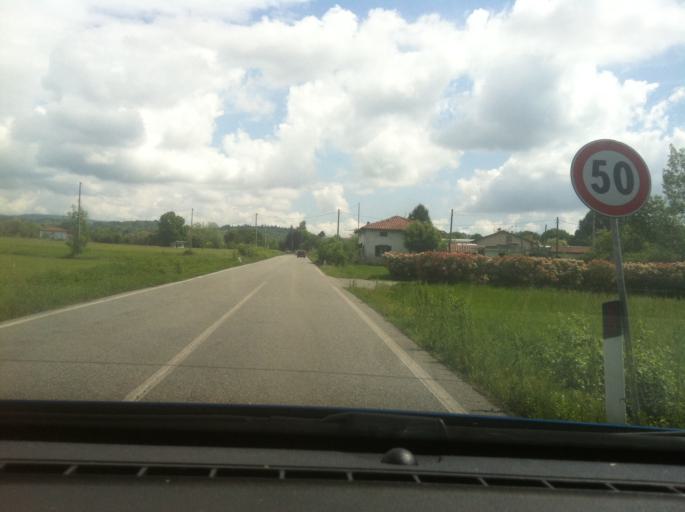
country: IT
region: Piedmont
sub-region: Provincia di Torino
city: Castellamonte
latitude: 45.3905
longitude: 7.7284
